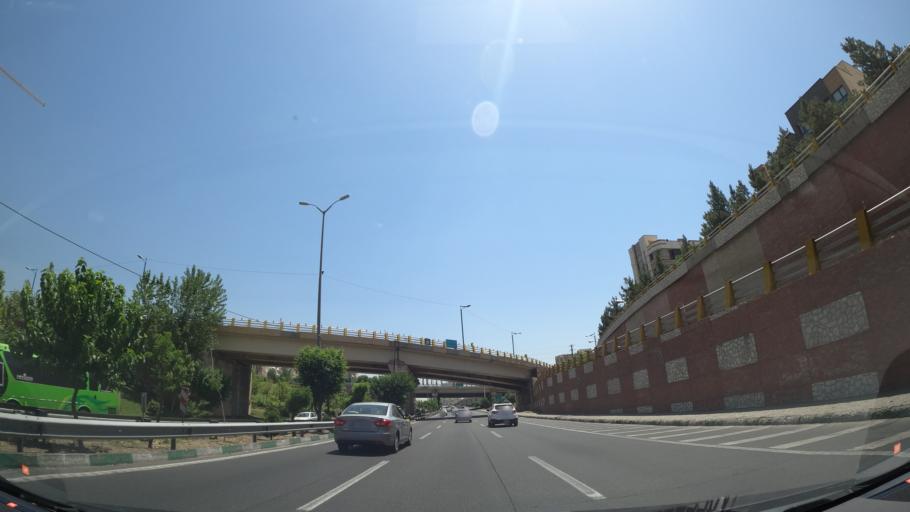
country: IR
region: Tehran
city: Tajrish
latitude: 35.7710
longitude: 51.3433
